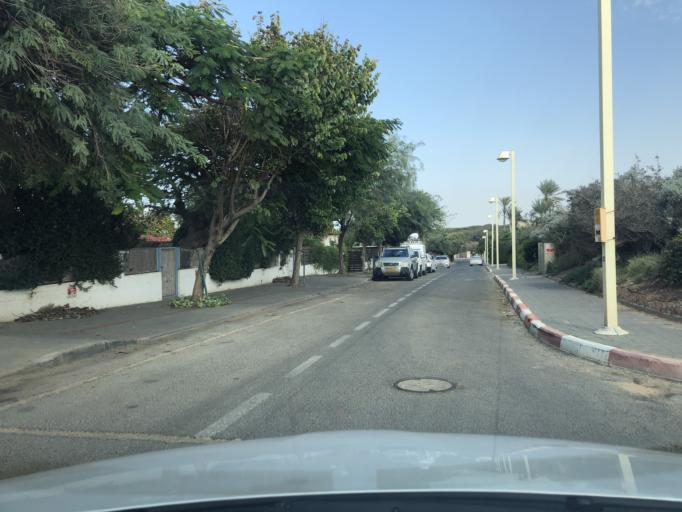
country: IL
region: Tel Aviv
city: Kefar Shemaryahu
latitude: 32.2145
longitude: 34.8157
